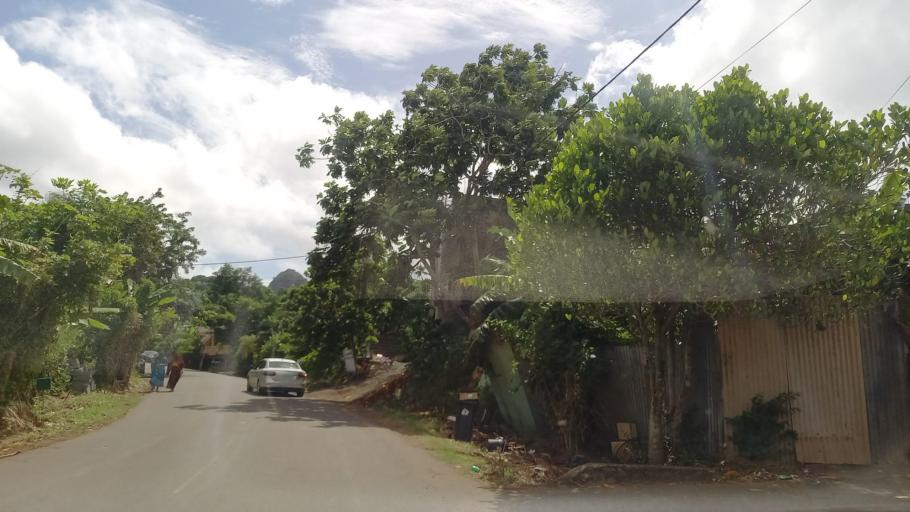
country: YT
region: Kani-Keli
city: Kani Keli
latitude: -12.9242
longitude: 45.1031
